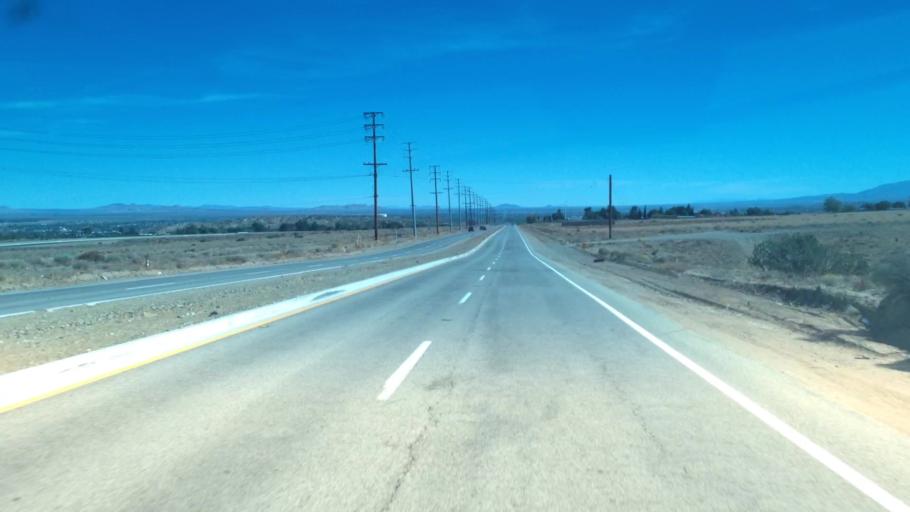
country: US
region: California
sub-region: Los Angeles County
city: Desert View Highlands
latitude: 34.5578
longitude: -118.1601
